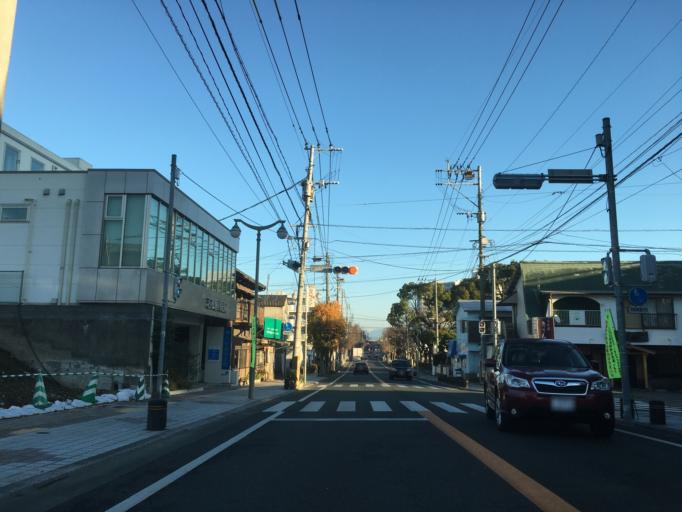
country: JP
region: Fukuoka
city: Kurume
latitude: 33.3232
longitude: 130.5090
